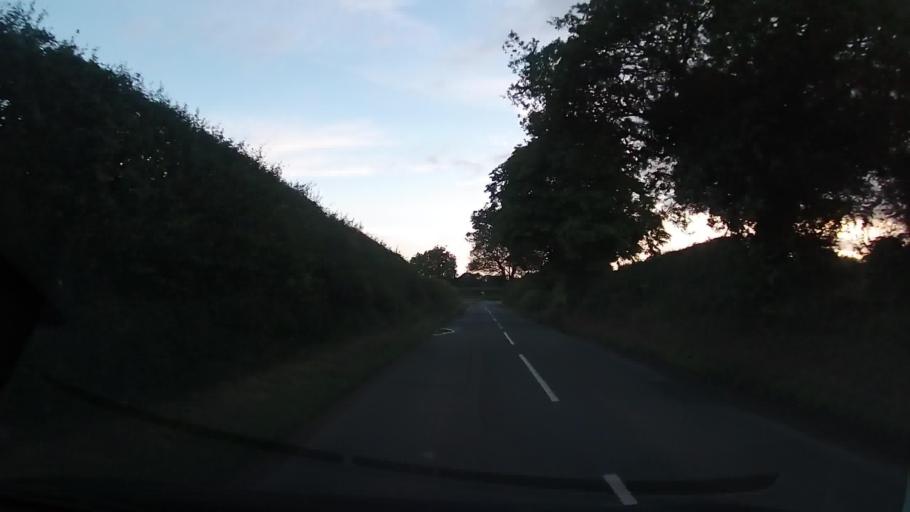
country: GB
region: England
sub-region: Shropshire
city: Prees
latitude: 52.8985
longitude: -2.6350
